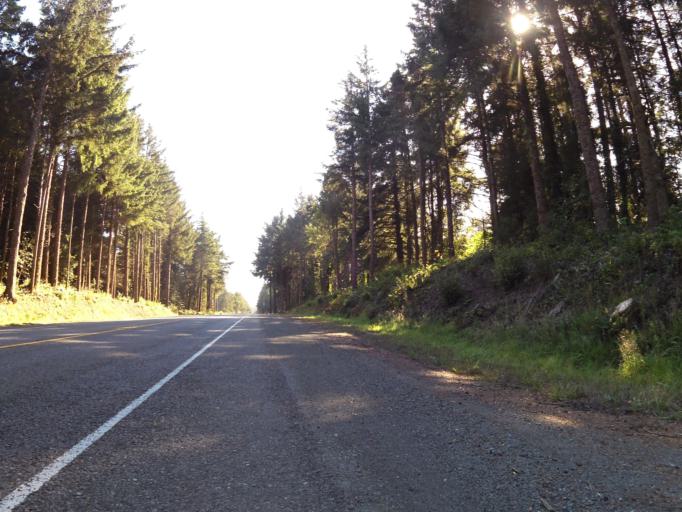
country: US
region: Oregon
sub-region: Curry County
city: Gold Beach
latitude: 42.4952
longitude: -124.4133
